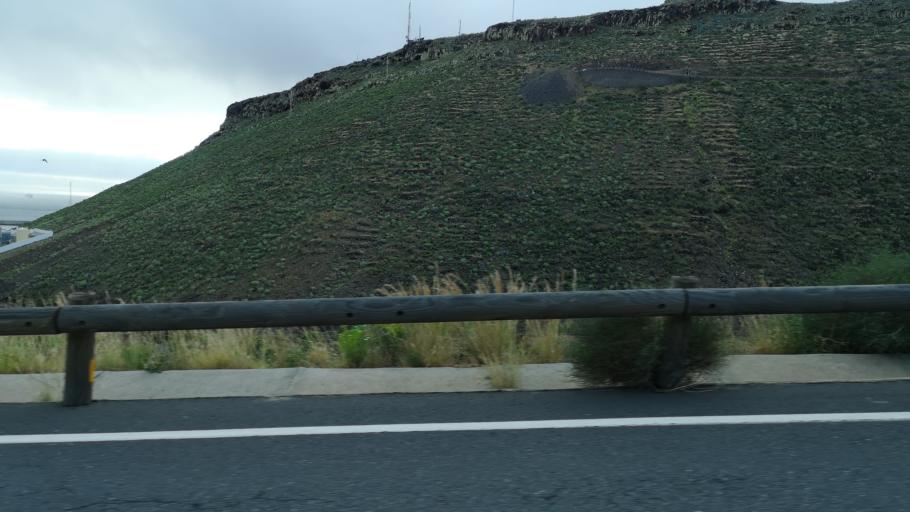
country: ES
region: Canary Islands
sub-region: Provincia de Santa Cruz de Tenerife
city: San Sebastian de la Gomera
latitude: 28.0895
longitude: -17.1231
